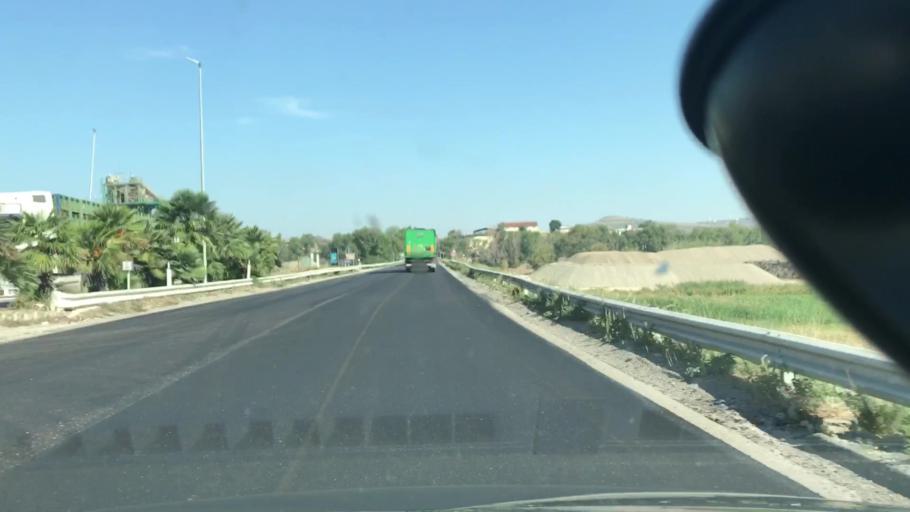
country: IT
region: Apulia
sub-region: Provincia di Foggia
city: Candela
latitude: 41.0938
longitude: 15.5942
